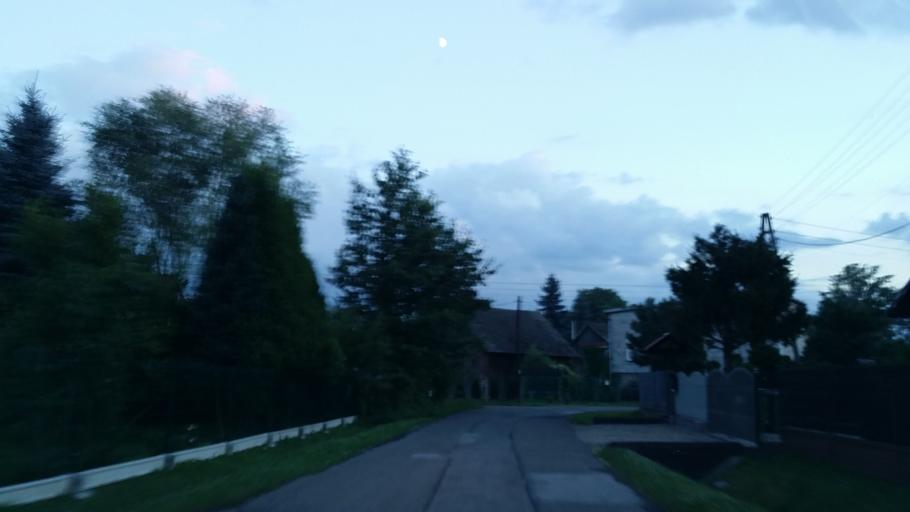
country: PL
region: Lesser Poland Voivodeship
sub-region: Powiat oswiecimski
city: Przeciszow
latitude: 50.0201
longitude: 19.3789
